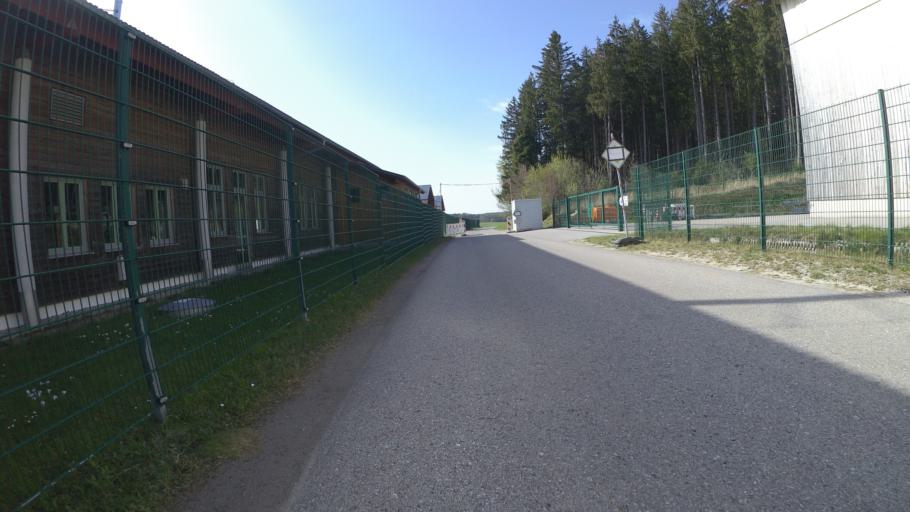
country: DE
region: Bavaria
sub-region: Upper Bavaria
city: Nussdorf
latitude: 47.9207
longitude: 12.5992
